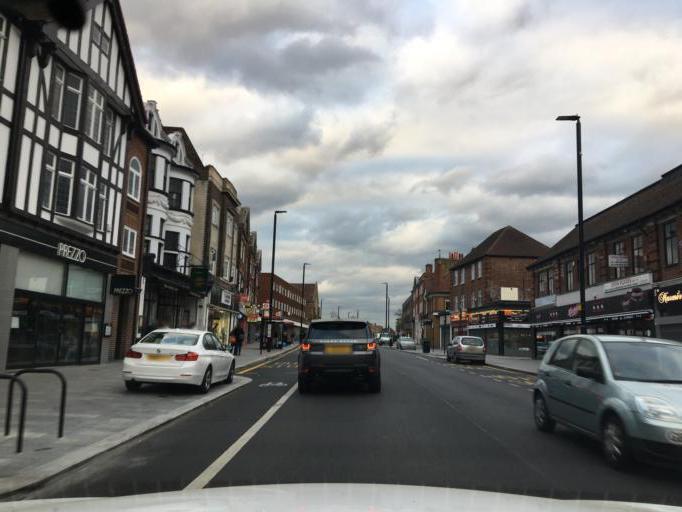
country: GB
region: England
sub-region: Greater London
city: Chislehurst
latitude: 51.4508
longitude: 0.0582
